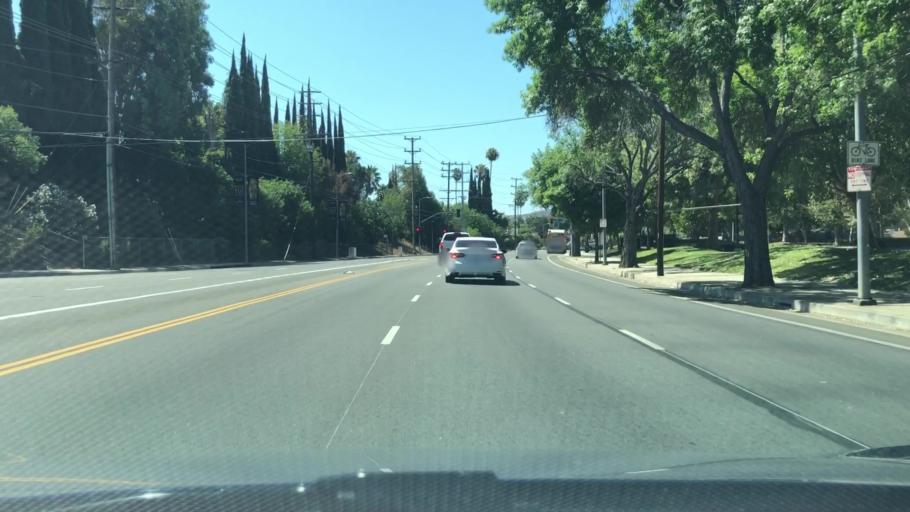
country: US
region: California
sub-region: Los Angeles County
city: Woodland Hills
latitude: 34.1745
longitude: -118.5886
